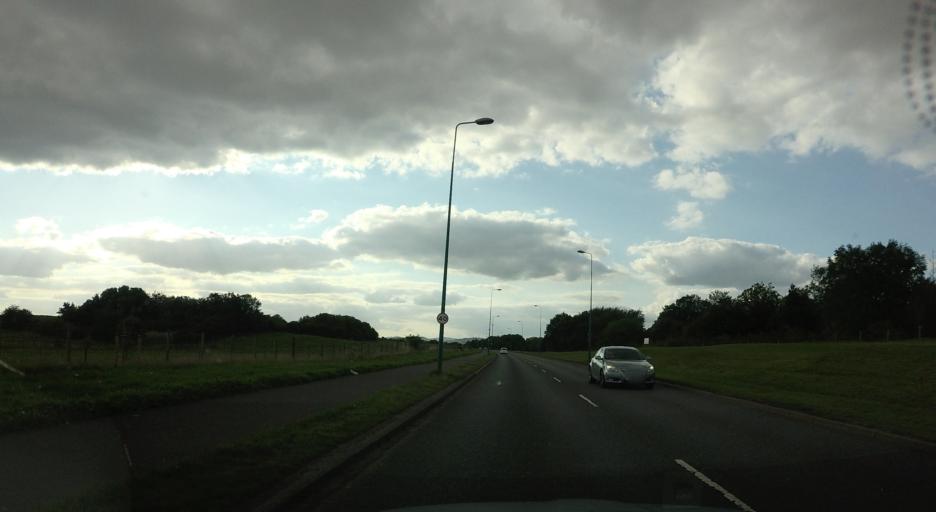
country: GB
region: Scotland
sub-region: Angus
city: Muirhead
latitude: 56.4569
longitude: -3.0380
